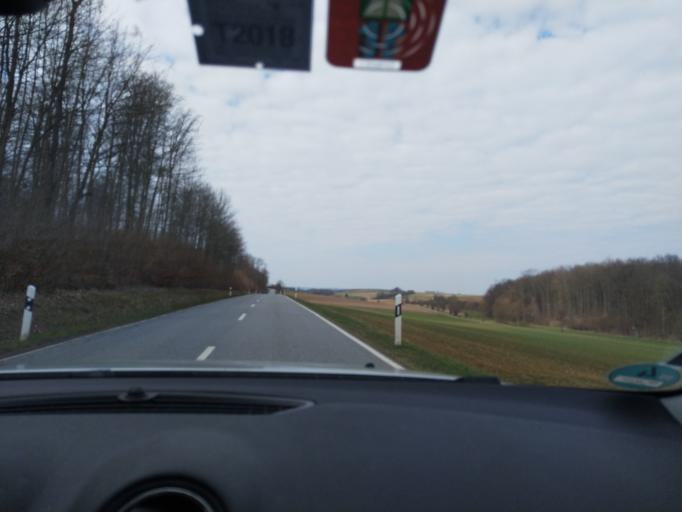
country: DE
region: Baden-Wuerttemberg
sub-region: Regierungsbezirk Stuttgart
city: Ilsfeld
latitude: 49.0382
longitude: 9.2314
